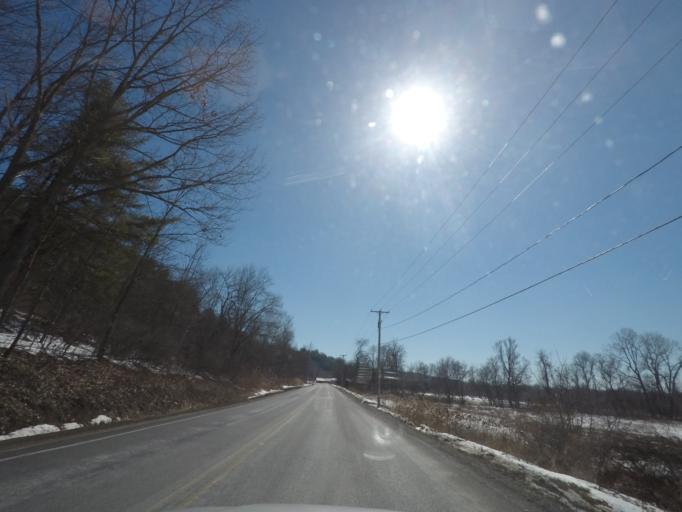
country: US
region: New York
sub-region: Saratoga County
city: Schuylerville
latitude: 43.1104
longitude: -73.5695
